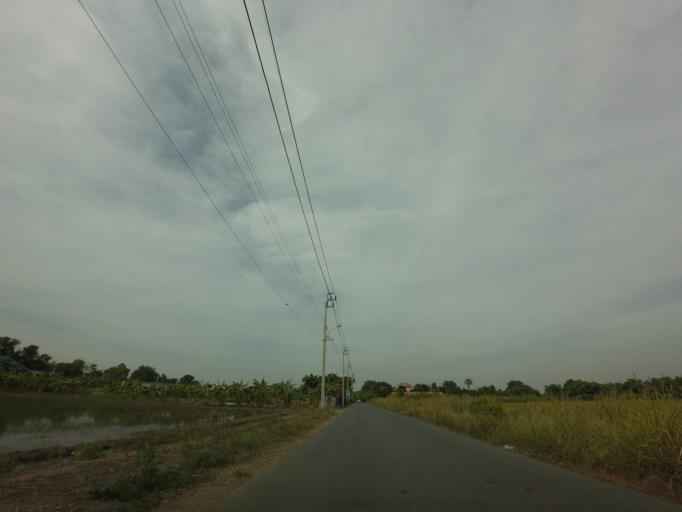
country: TH
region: Pathum Thani
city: Lam Luk Ka
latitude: 13.8900
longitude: 100.7039
